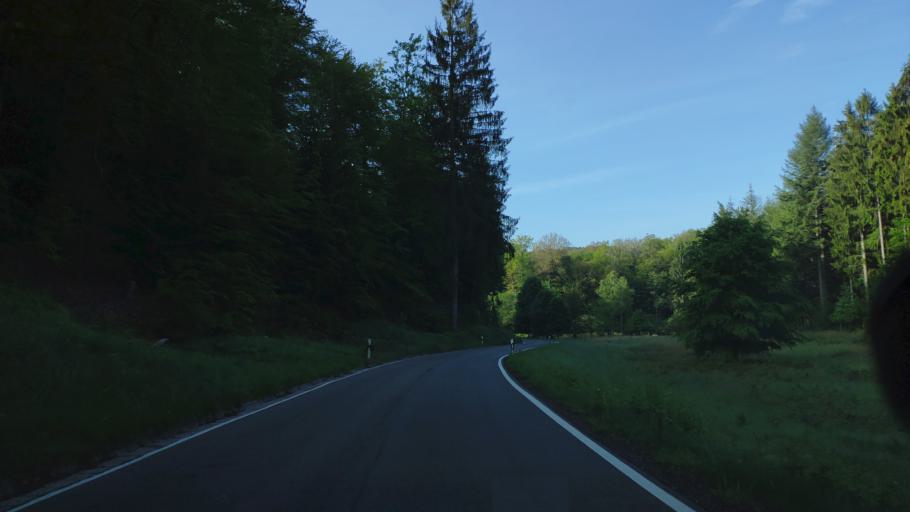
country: DE
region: Rheinland-Pfalz
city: Ludwigswinkel
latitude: 49.1105
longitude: 7.6709
